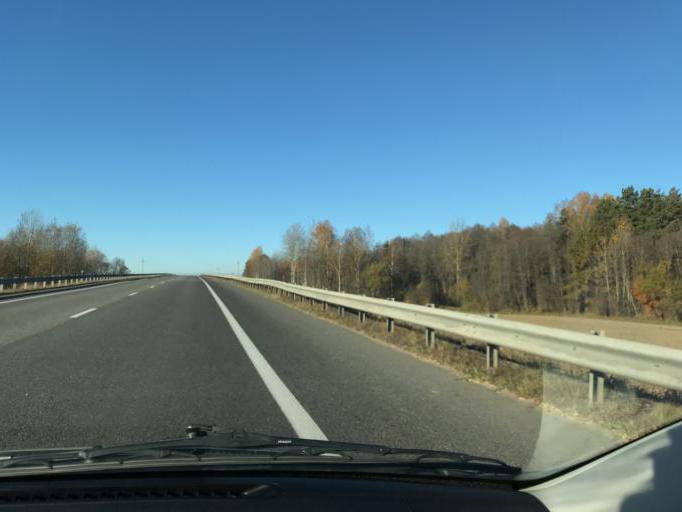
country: BY
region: Vitebsk
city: Vitebsk
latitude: 55.1034
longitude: 30.1703
